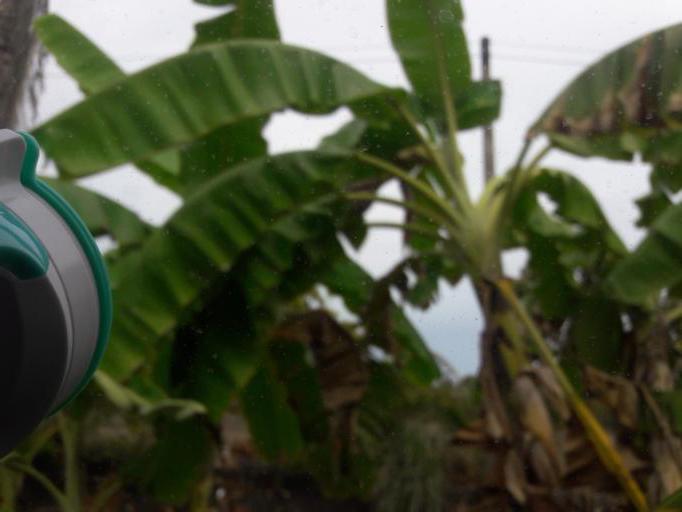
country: TH
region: Ratchaburi
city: Damnoen Saduak
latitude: 13.5235
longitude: 100.0062
